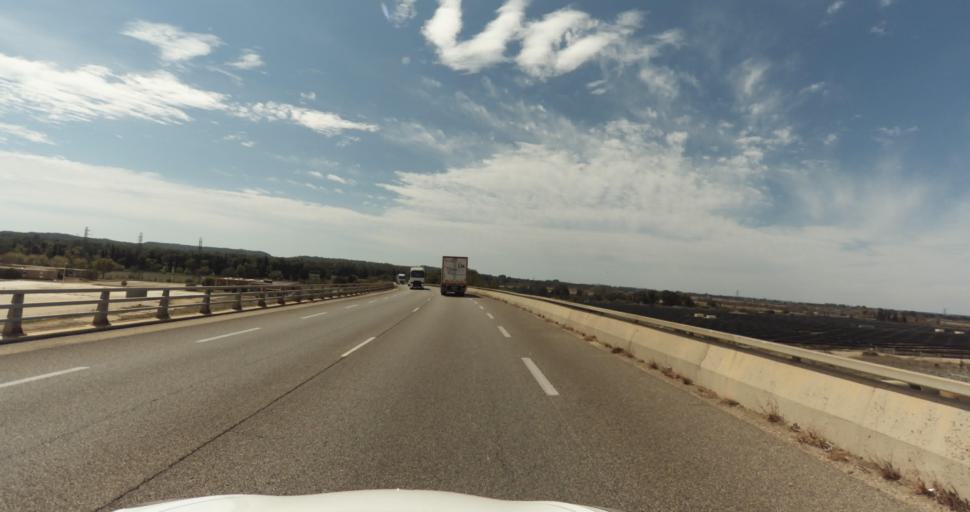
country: FR
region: Provence-Alpes-Cote d'Azur
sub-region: Departement des Bouches-du-Rhone
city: Miramas
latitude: 43.5807
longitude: 4.9845
